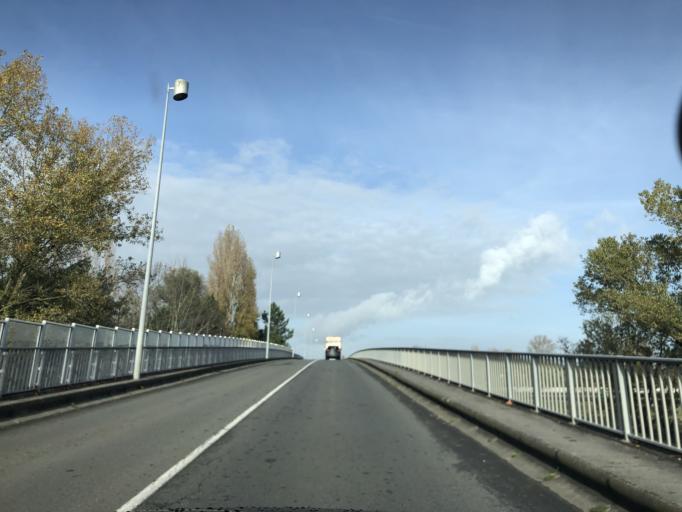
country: FR
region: Aquitaine
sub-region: Departement de la Gironde
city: Le Bouscat
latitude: 44.8871
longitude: -0.5877
